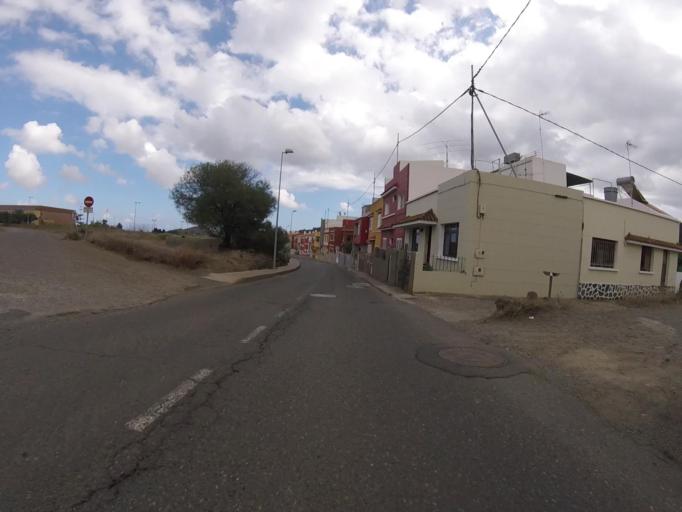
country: ES
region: Canary Islands
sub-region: Provincia de Las Palmas
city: Santa Brigida
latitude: 28.0387
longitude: -15.4936
